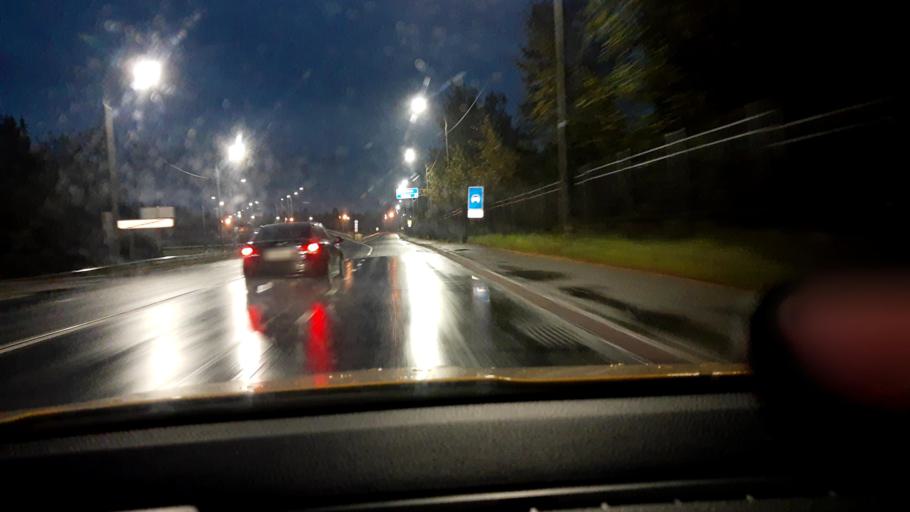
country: RU
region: Moskovskaya
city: Krasnoznamensk
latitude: 55.6057
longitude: 37.0511
